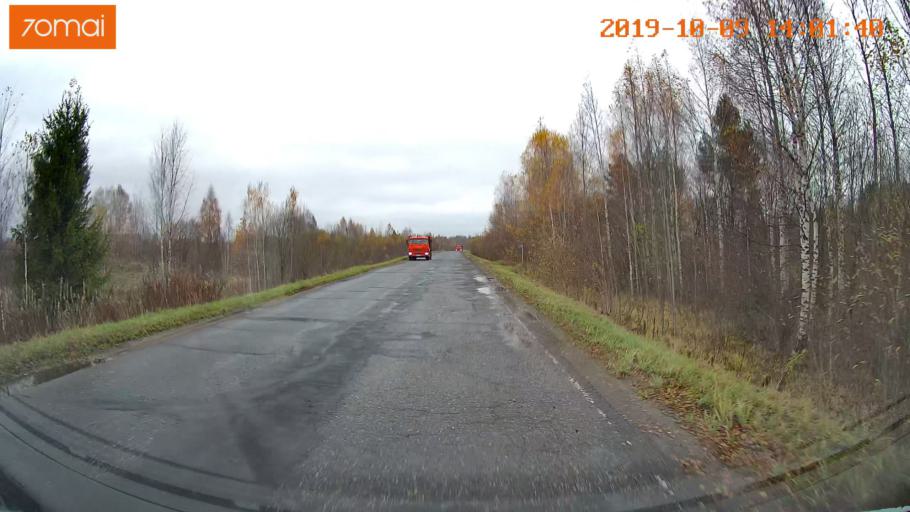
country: RU
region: Kostroma
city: Buy
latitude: 58.4449
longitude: 41.3494
